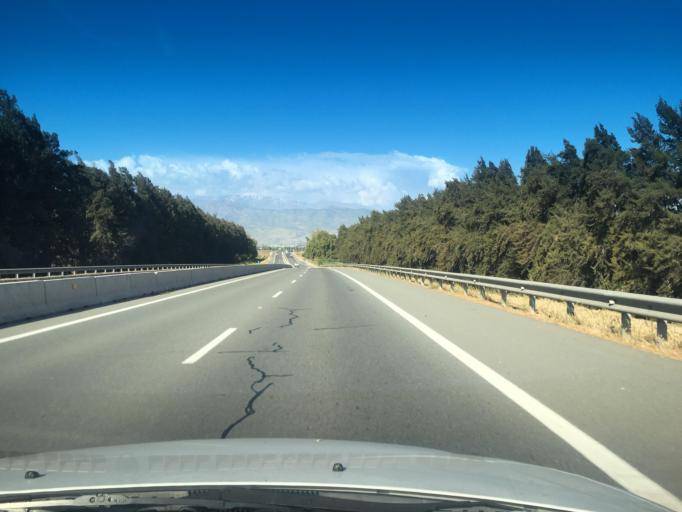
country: CL
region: Santiago Metropolitan
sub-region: Provincia de Chacabuco
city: Chicureo Abajo
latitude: -33.2935
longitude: -70.7115
